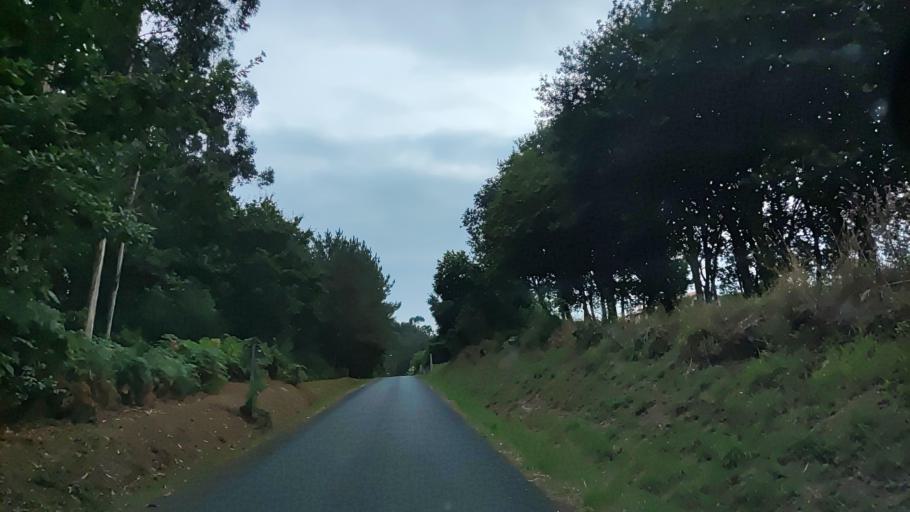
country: ES
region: Galicia
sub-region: Provincia da Coruna
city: Padron
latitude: 42.7176
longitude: -8.6835
